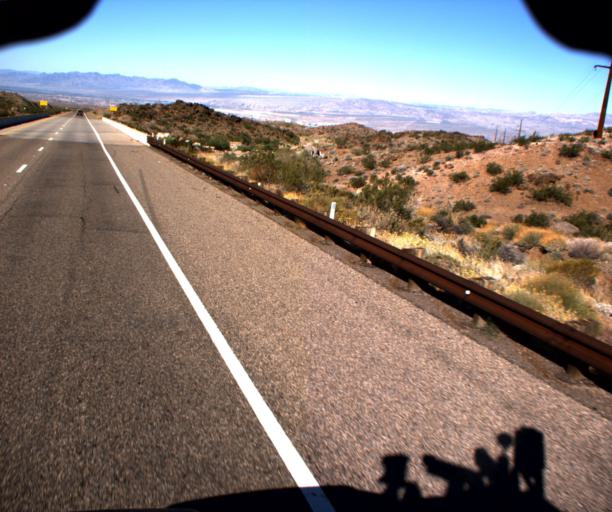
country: US
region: Nevada
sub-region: Clark County
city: Laughlin
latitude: 35.1934
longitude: -114.4409
